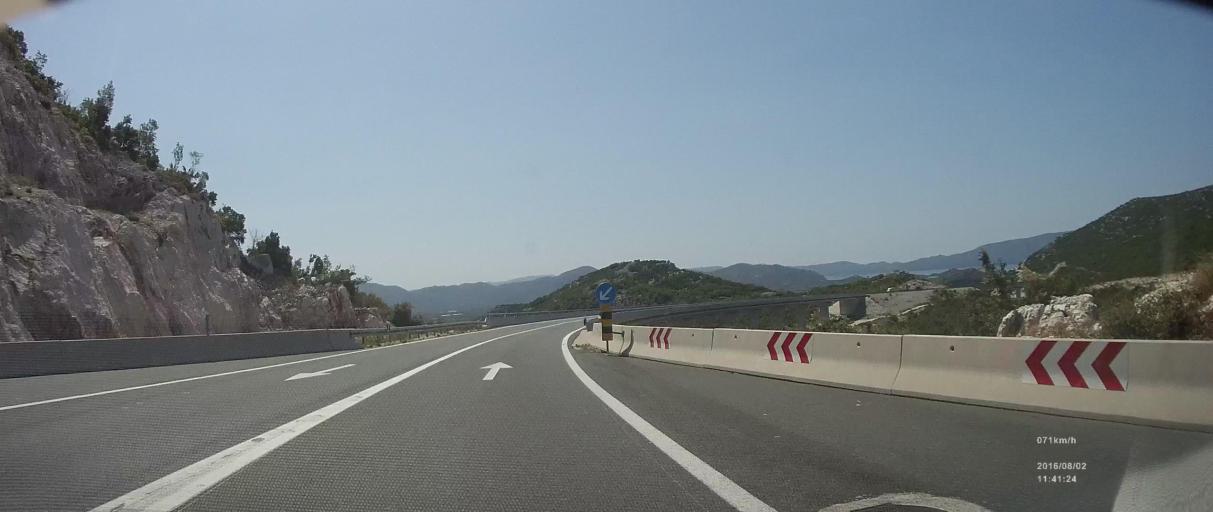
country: HR
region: Dubrovacko-Neretvanska
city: Komin
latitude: 43.0640
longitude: 17.4958
